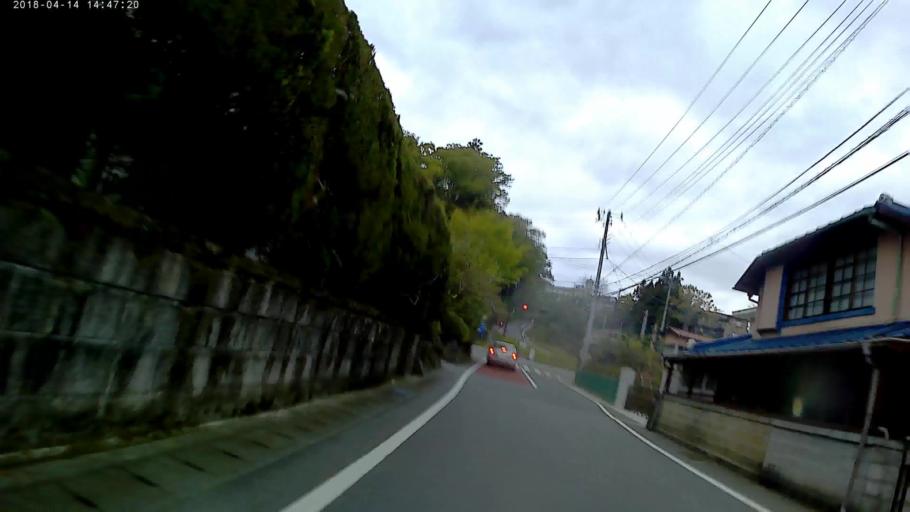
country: JP
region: Shizuoka
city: Gotemba
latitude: 35.3658
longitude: 138.9816
